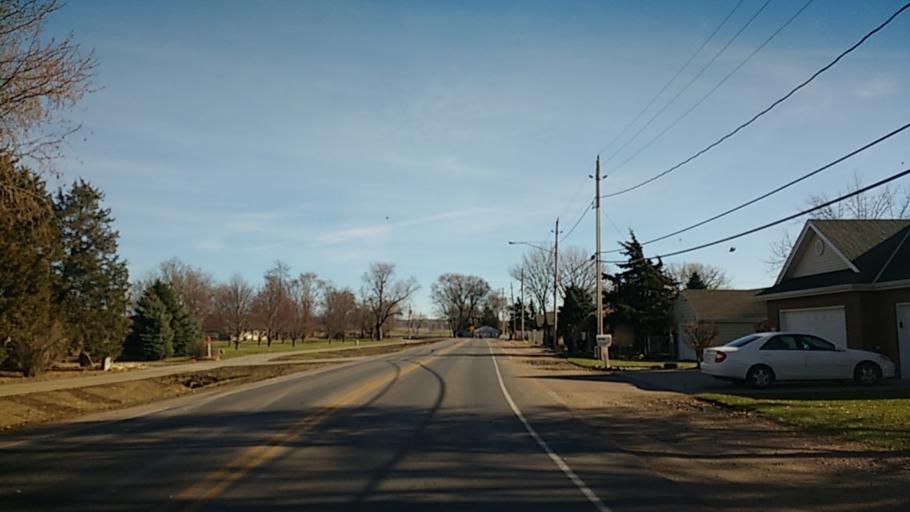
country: US
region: South Dakota
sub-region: Union County
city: North Sioux City
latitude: 42.5509
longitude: -96.5141
